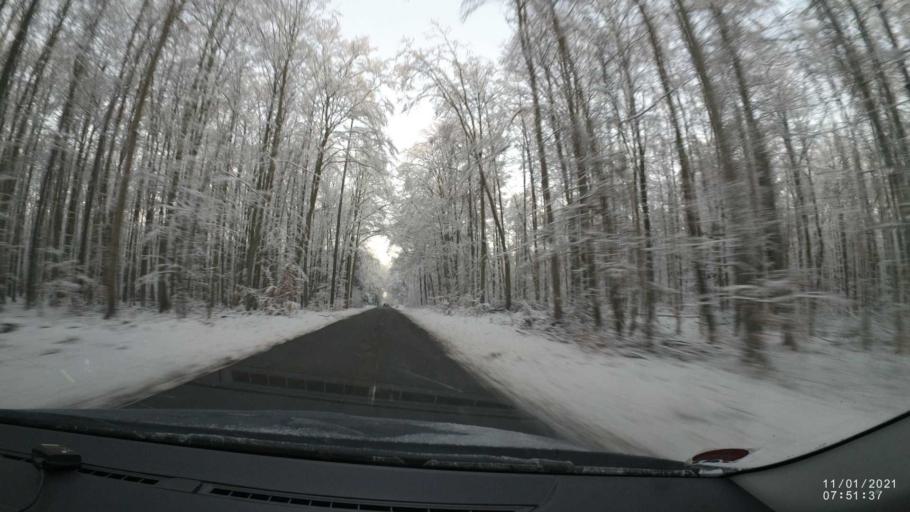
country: CZ
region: South Moravian
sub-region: Okres Blansko
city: Adamov
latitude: 49.2846
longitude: 16.6552
